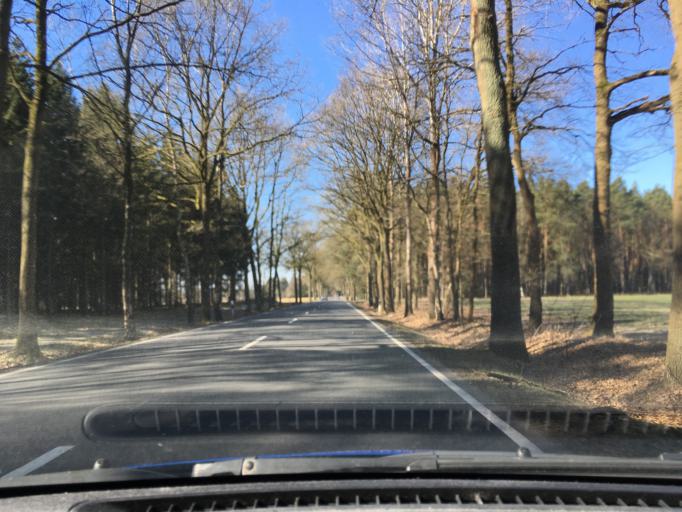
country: DE
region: Lower Saxony
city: Brockel
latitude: 53.0912
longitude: 9.5484
